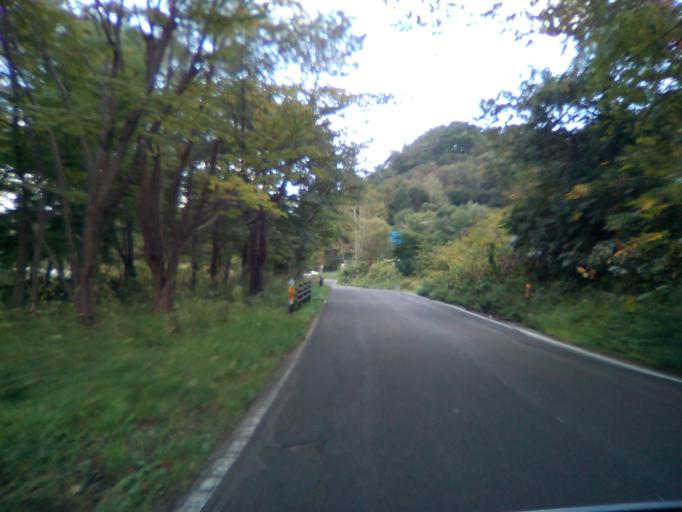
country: JP
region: Hokkaido
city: Date
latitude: 42.5803
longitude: 140.7962
